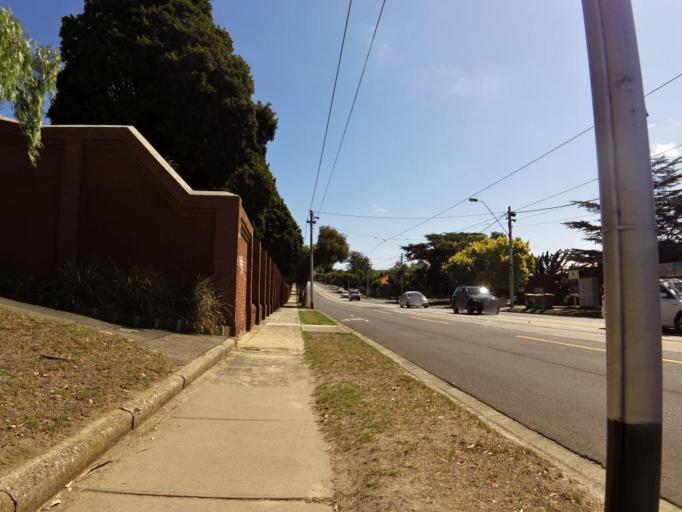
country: AU
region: Victoria
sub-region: Boroondara
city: Kew East
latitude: -37.8014
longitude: 145.0460
